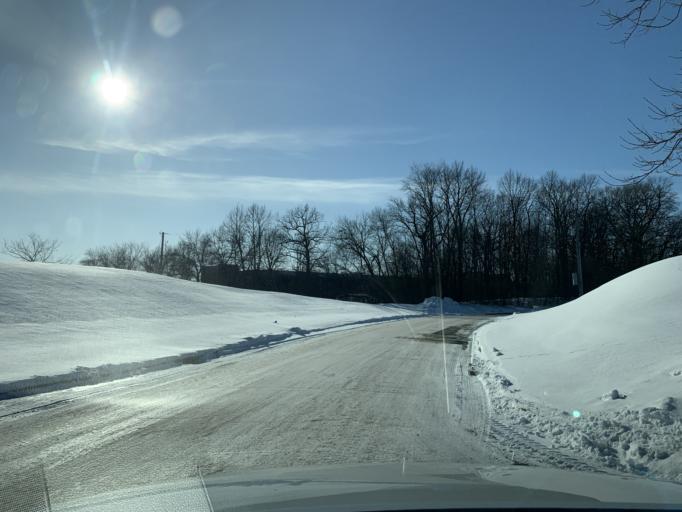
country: US
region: Minnesota
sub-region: Scott County
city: Savage
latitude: 44.8233
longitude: -93.3476
